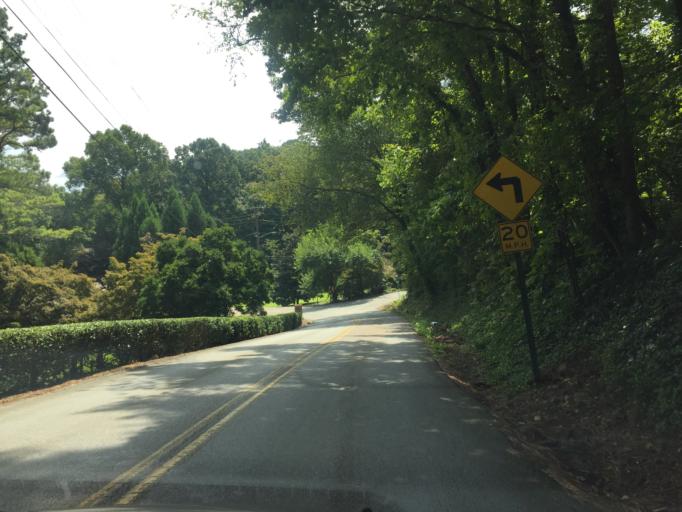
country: US
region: Tennessee
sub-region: Hamilton County
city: East Chattanooga
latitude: 35.0974
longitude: -85.2046
